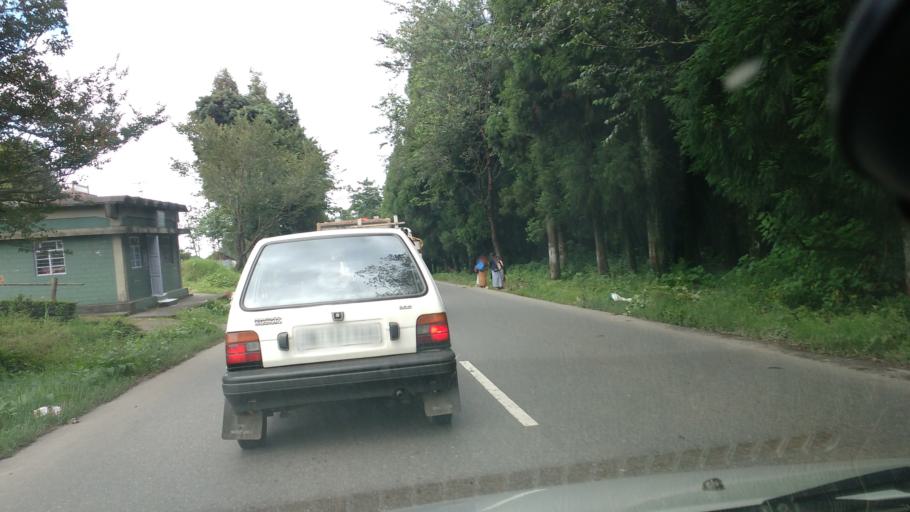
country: IN
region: Meghalaya
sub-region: East Khasi Hills
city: Shillong
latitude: 25.5509
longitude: 91.8424
